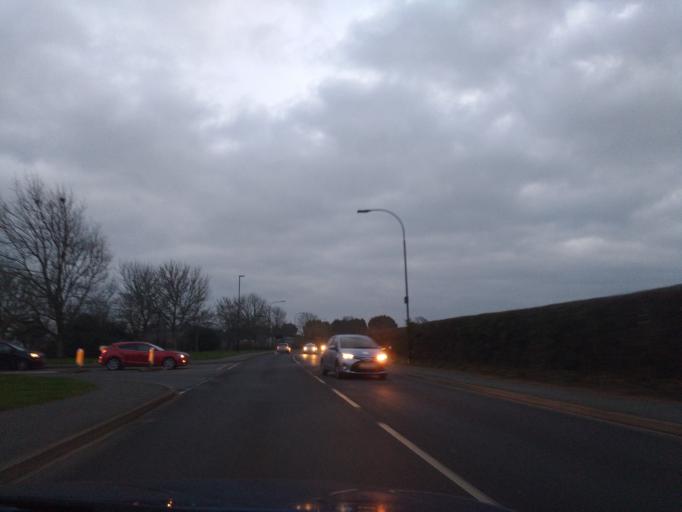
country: GB
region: England
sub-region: Isle of Wight
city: Northwood
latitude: 50.7479
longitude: -1.3123
